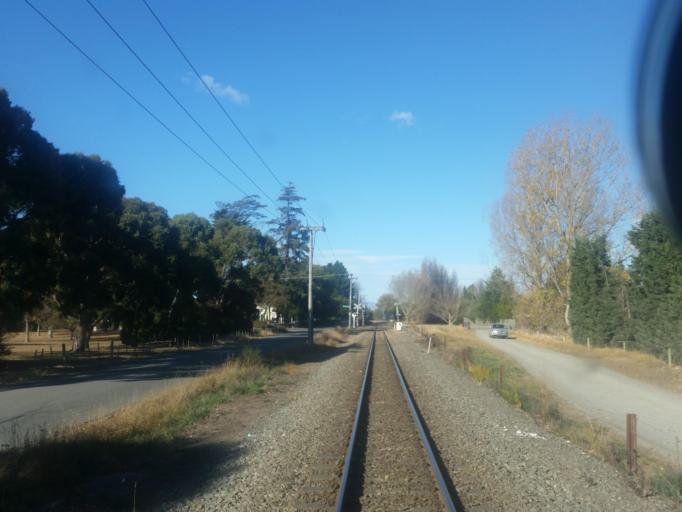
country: NZ
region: Canterbury
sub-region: Waimakariri District
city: Woodend
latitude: -43.2901
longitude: 172.5973
